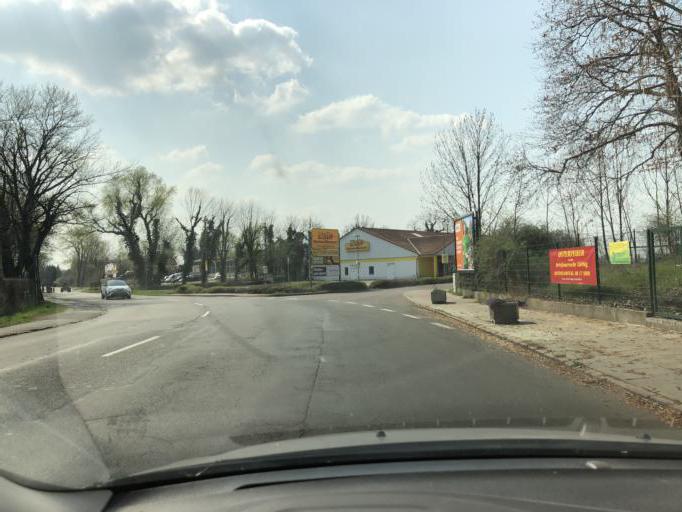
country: DE
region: Saxony-Anhalt
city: Zorbig
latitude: 51.6275
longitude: 12.1117
